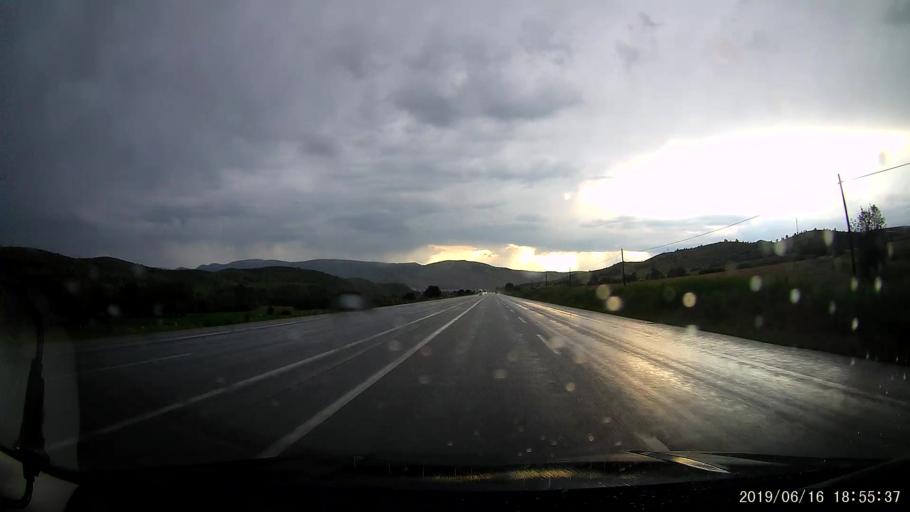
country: TR
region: Erzincan
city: Refahiye
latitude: 39.9009
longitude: 38.8235
